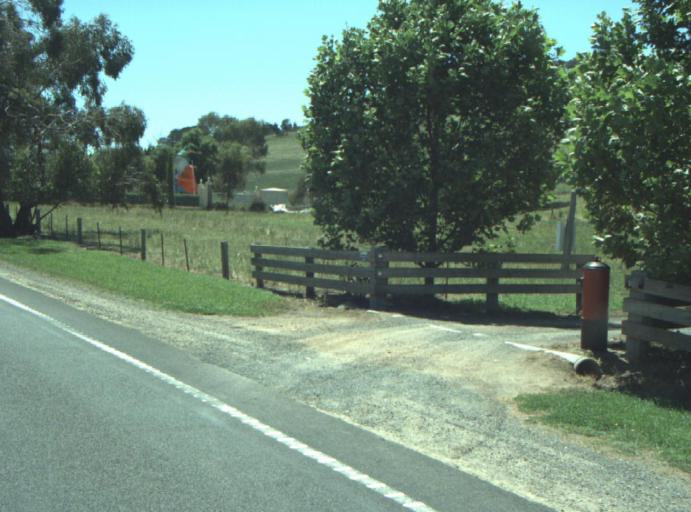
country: AU
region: Victoria
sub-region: Greater Geelong
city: Lara
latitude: -37.8910
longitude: 144.2559
